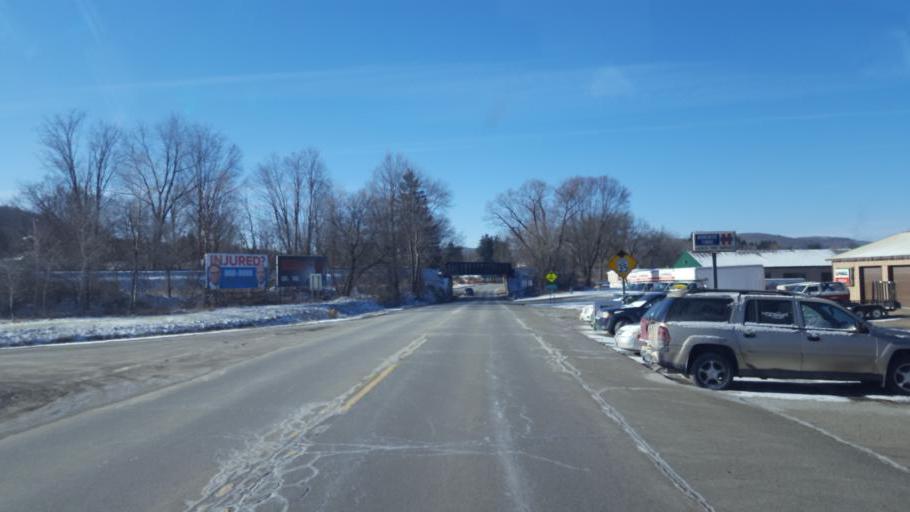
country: US
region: New York
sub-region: Allegany County
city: Wellsville
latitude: 42.1235
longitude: -77.9283
